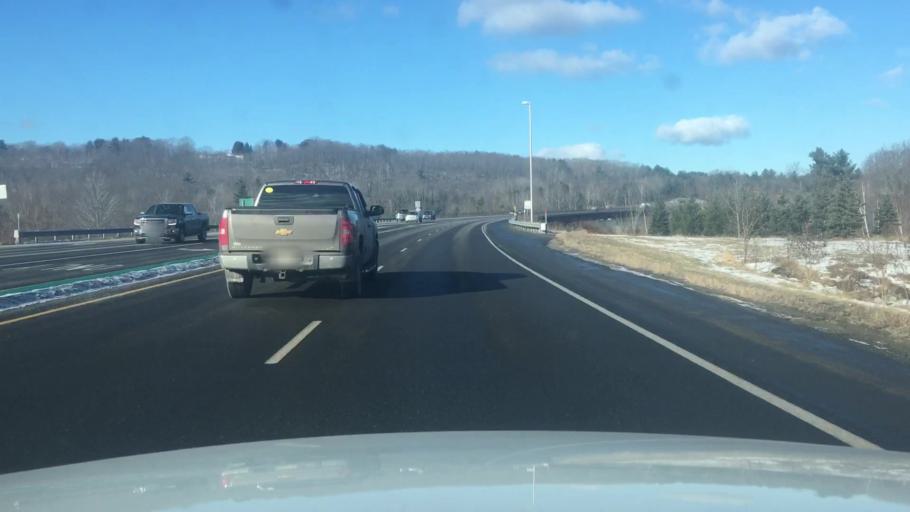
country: US
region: Maine
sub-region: Kennebec County
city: Augusta
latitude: 44.3336
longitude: -69.7614
